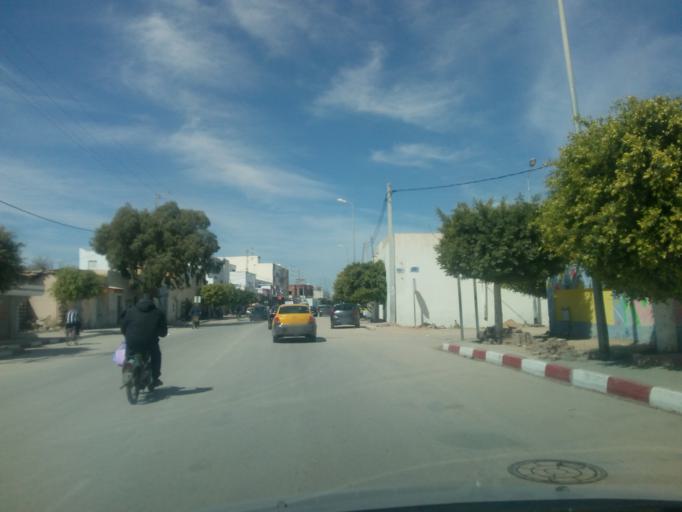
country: TN
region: Safaqis
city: Sfax
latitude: 34.7675
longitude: 10.7087
